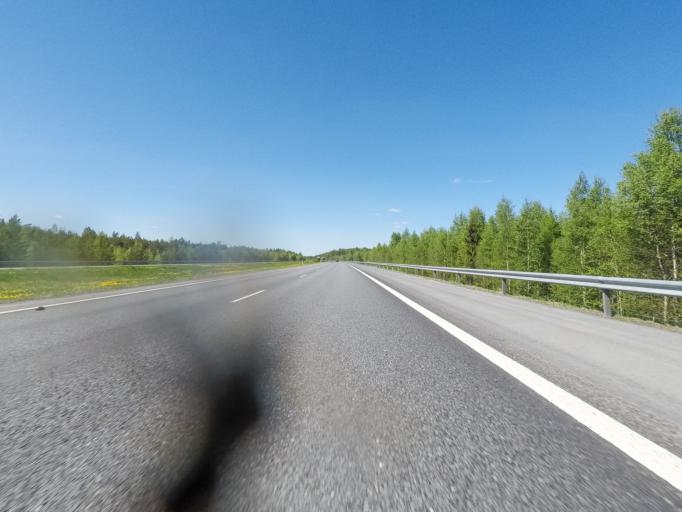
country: FI
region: Haeme
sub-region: Haemeenlinna
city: Kalvola
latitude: 61.1226
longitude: 24.1219
